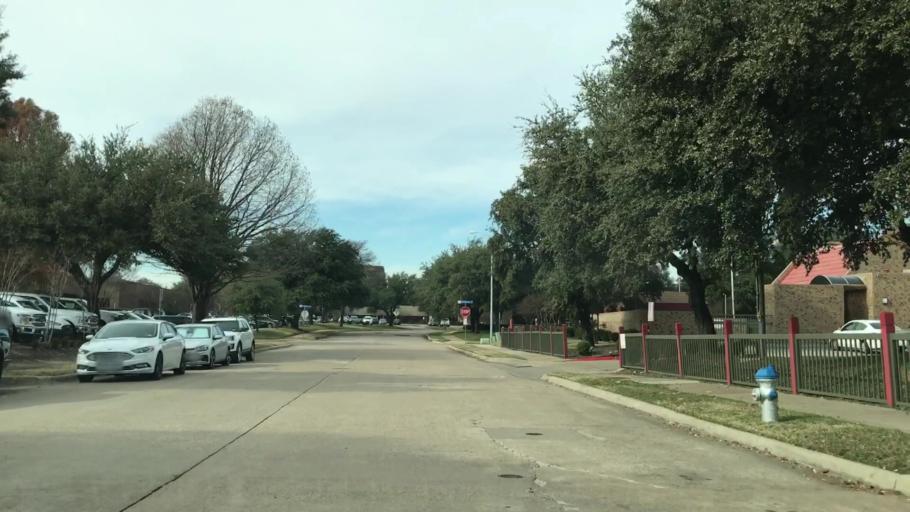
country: US
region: Texas
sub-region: Dallas County
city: Richardson
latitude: 32.9733
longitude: -96.7208
